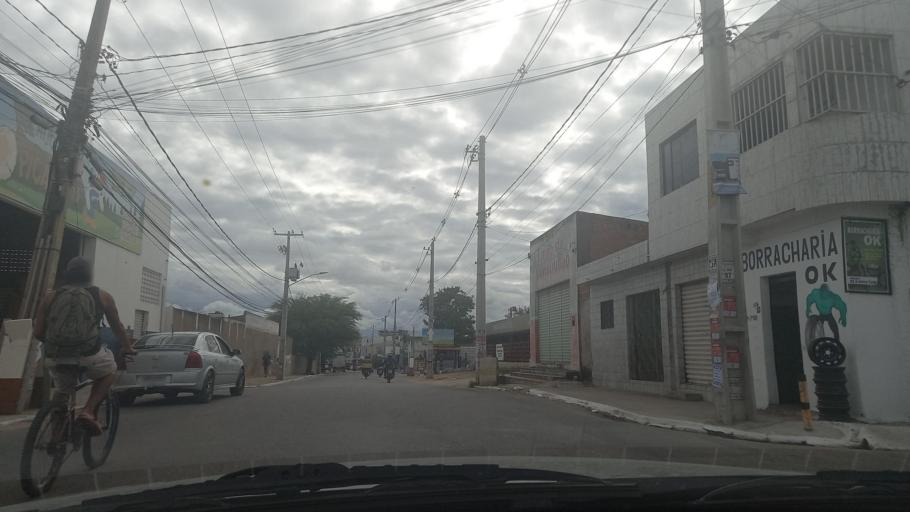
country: BR
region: Pernambuco
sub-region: Caruaru
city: Caruaru
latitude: -8.2871
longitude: -35.9904
